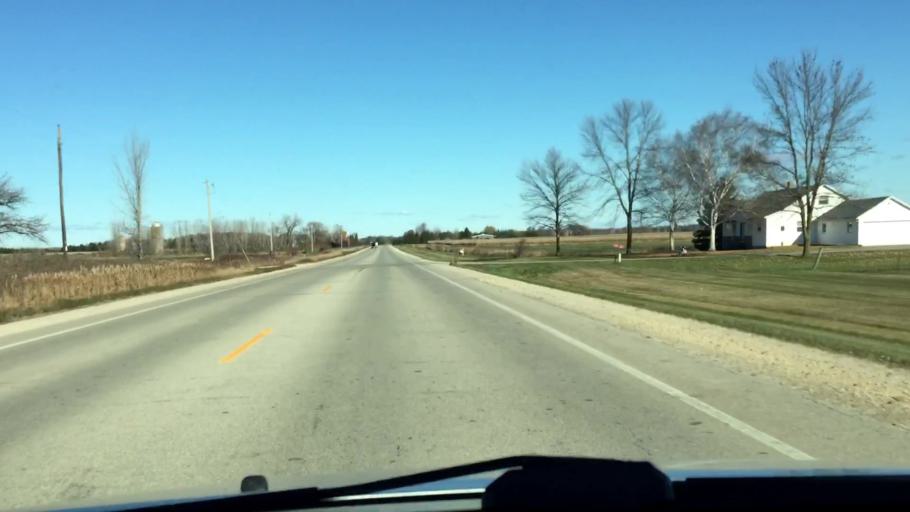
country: US
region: Wisconsin
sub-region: Brown County
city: Pulaski
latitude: 44.7342
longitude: -88.2474
